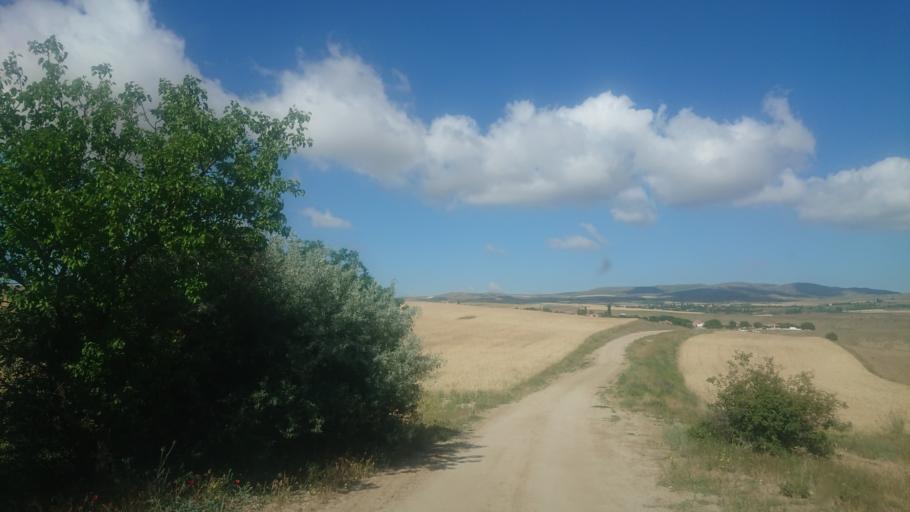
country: TR
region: Aksaray
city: Agacoren
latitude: 38.9064
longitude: 33.8669
